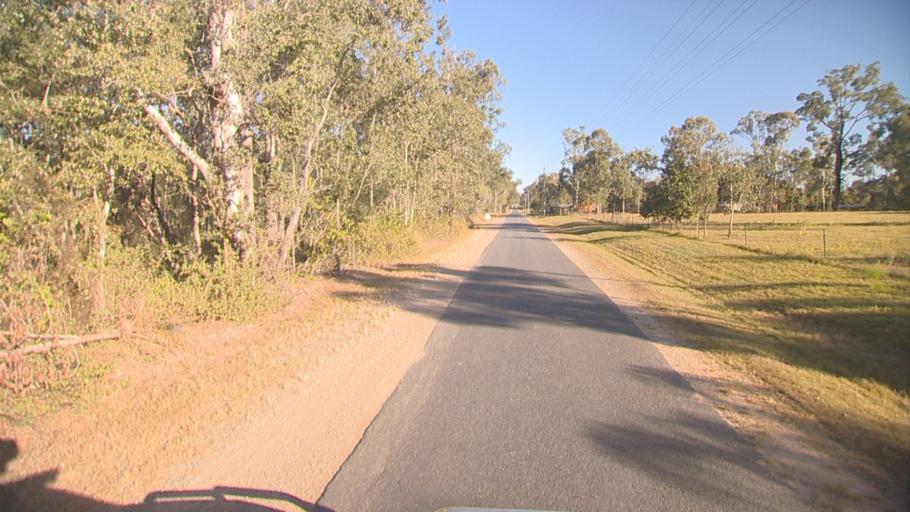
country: AU
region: Queensland
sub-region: Logan
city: North Maclean
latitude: -27.7826
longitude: 153.0396
